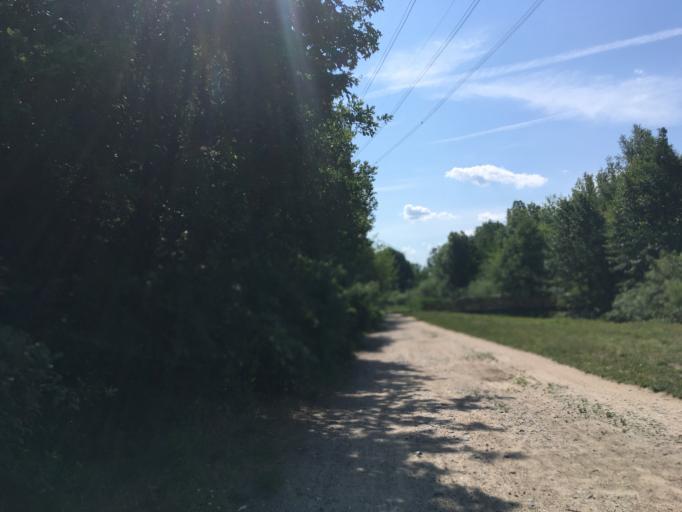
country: DE
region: Brandenburg
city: Ahrensfelde
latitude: 52.5600
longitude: 13.5809
